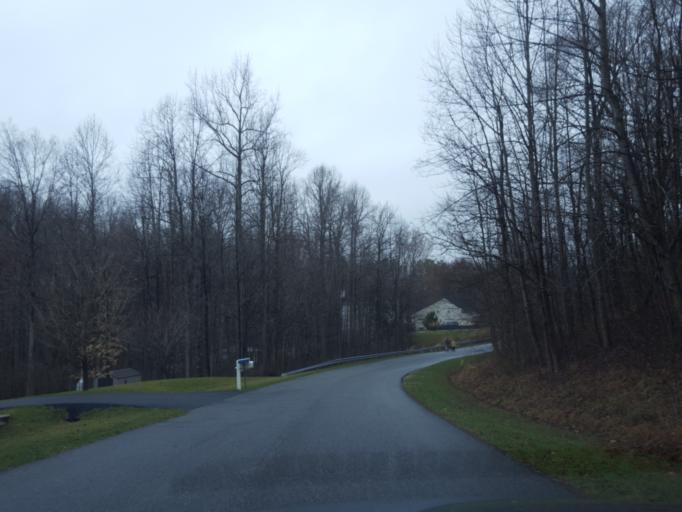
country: US
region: Maryland
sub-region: Calvert County
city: Huntingtown
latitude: 38.6086
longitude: -76.5380
